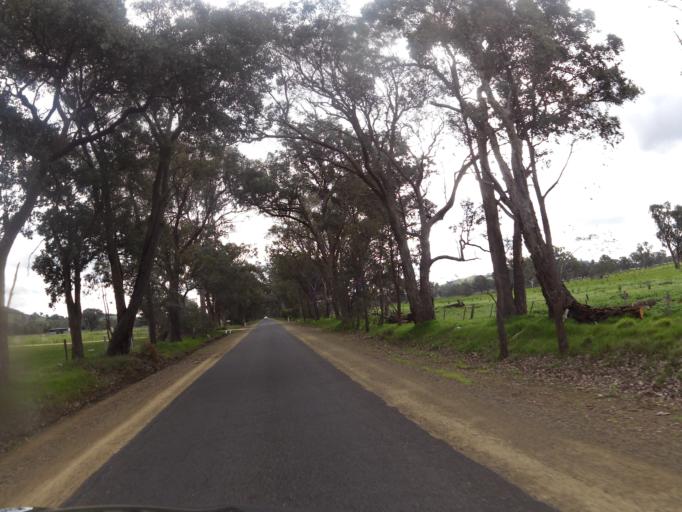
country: AU
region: Victoria
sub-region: Benalla
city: Benalla
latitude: -36.6799
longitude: 145.9697
